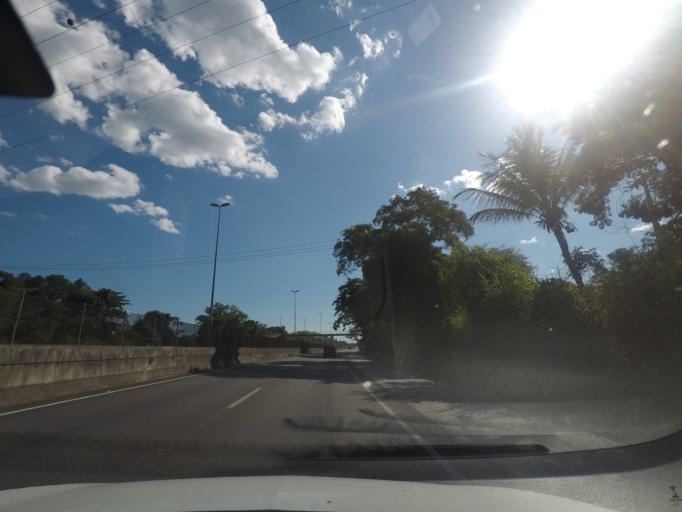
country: BR
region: Rio de Janeiro
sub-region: Guapimirim
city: Guapimirim
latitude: -22.6050
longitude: -43.0266
